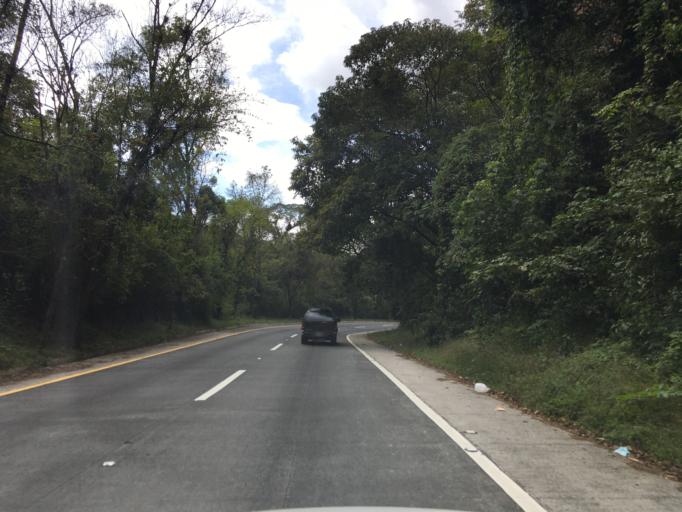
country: GT
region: Sacatepequez
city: Santa Lucia Milpas Altas
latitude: 14.5604
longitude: -90.6911
